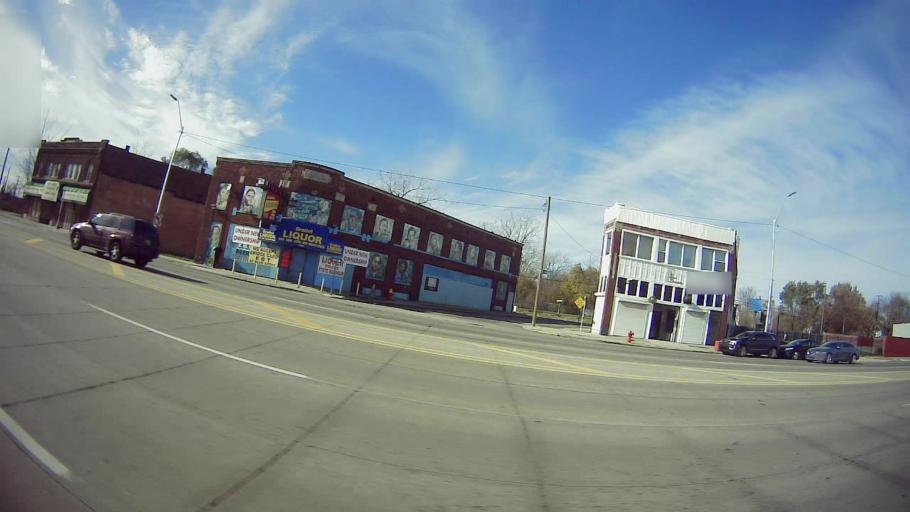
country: US
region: Michigan
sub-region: Wayne County
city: Detroit
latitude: 42.3595
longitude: -83.0273
